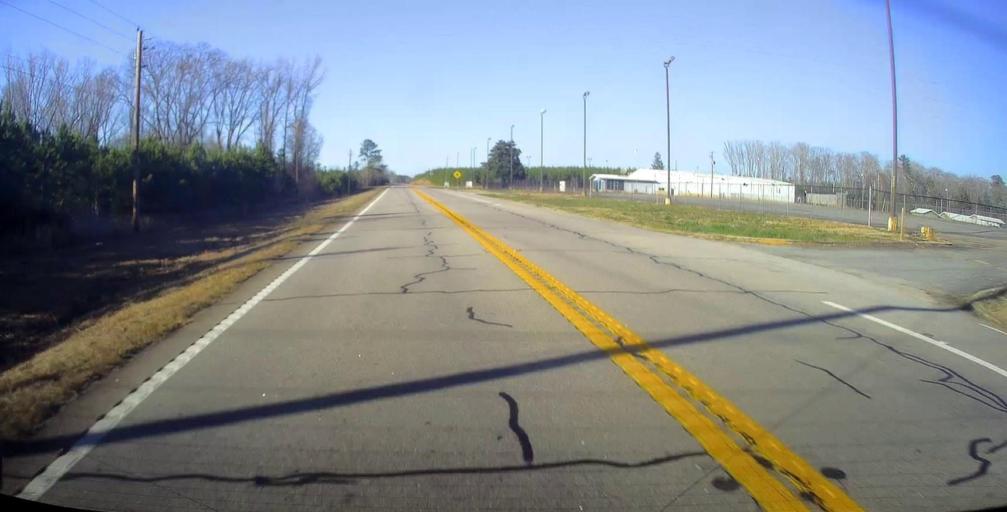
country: US
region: Georgia
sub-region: Meriwether County
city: Manchester
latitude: 32.8747
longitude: -84.5971
